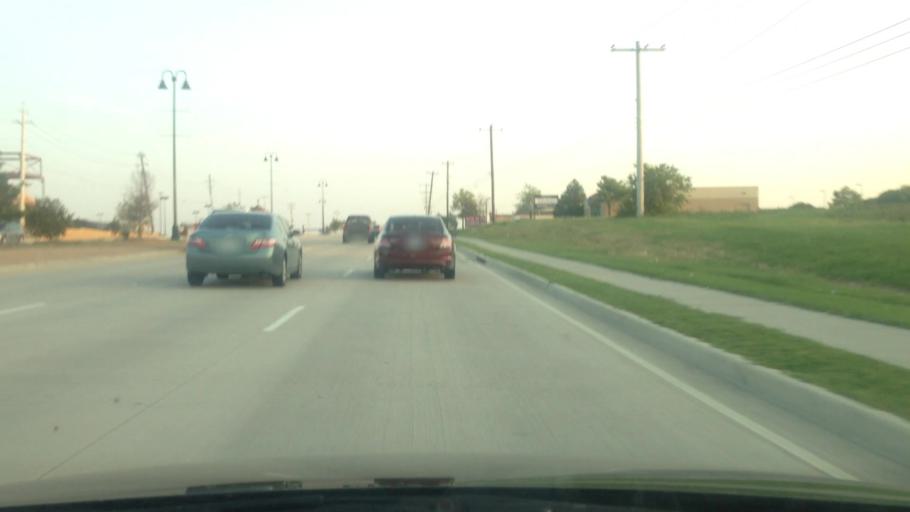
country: US
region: Texas
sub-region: Denton County
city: The Colony
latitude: 33.0839
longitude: -96.8931
